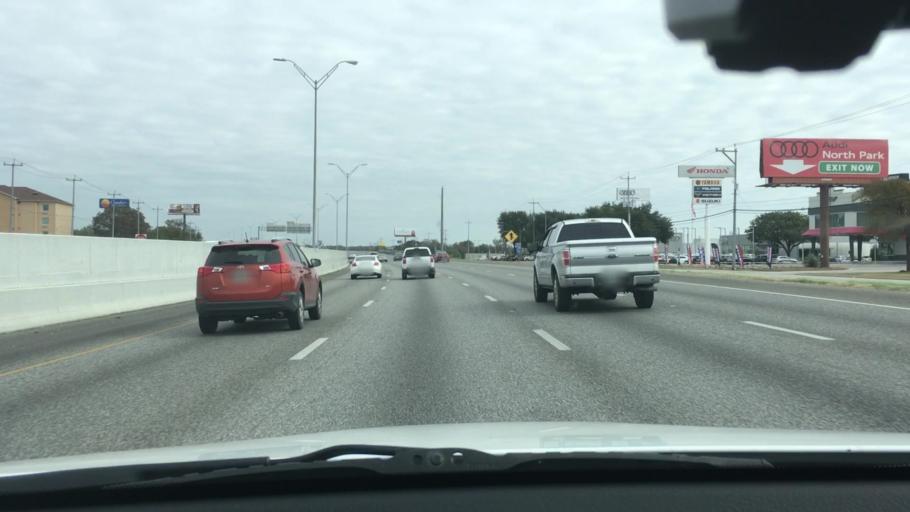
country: US
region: Texas
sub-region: Bexar County
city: Selma
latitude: 29.5811
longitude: -98.3109
